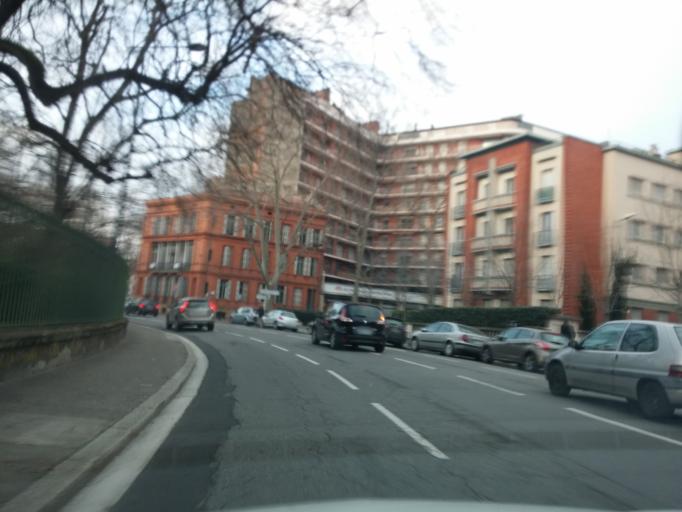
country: FR
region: Midi-Pyrenees
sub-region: Departement de la Haute-Garonne
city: Toulouse
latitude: 43.5952
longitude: 1.4538
